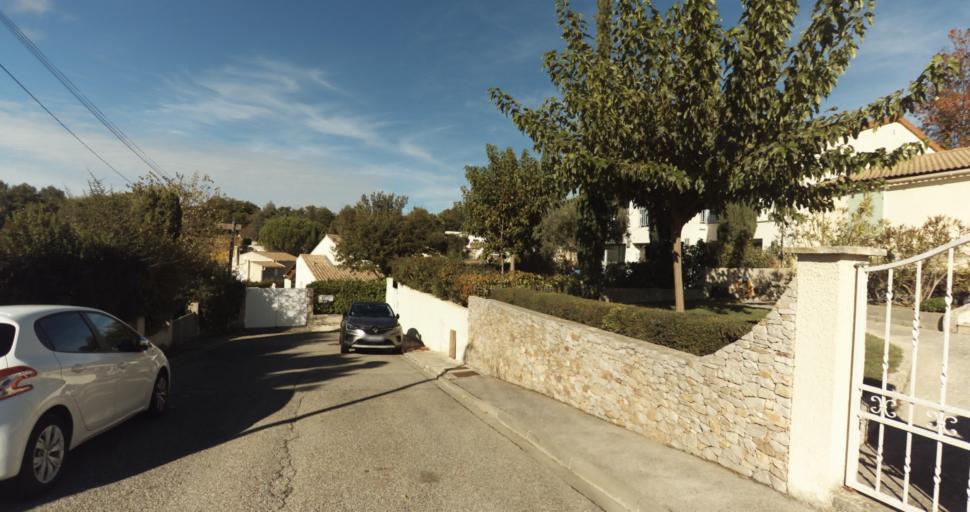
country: FR
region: Provence-Alpes-Cote d'Azur
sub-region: Departement des Bouches-du-Rhone
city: Venelles
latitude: 43.5977
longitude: 5.4762
